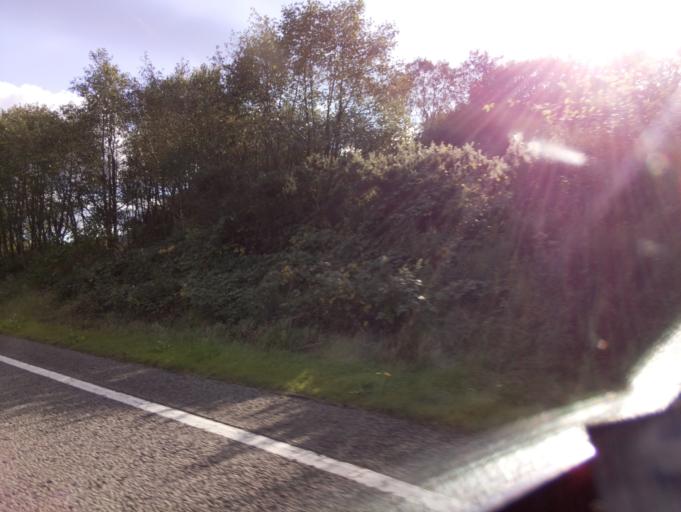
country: GB
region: Wales
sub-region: Merthyr Tydfil County Borough
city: Merthyr Tydfil
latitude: 51.7387
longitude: -3.3838
